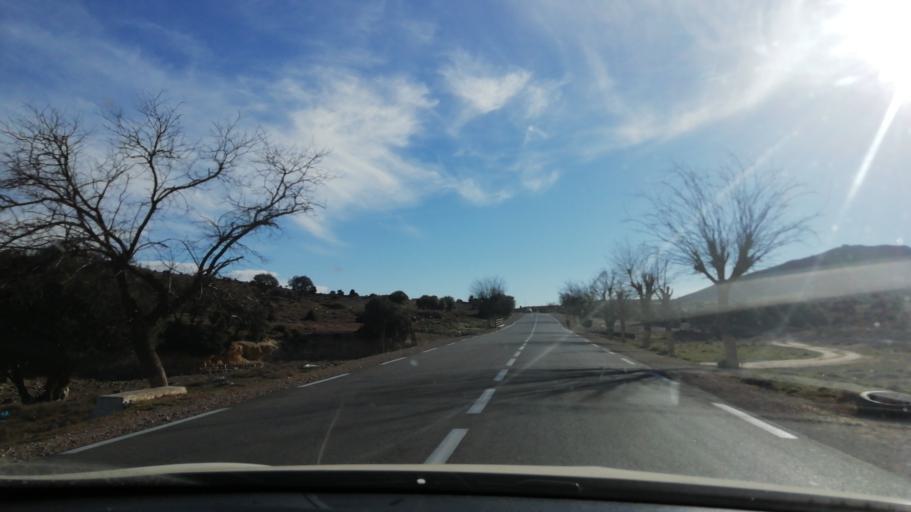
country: DZ
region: Tlemcen
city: Sebdou
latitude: 34.5802
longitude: -1.3189
